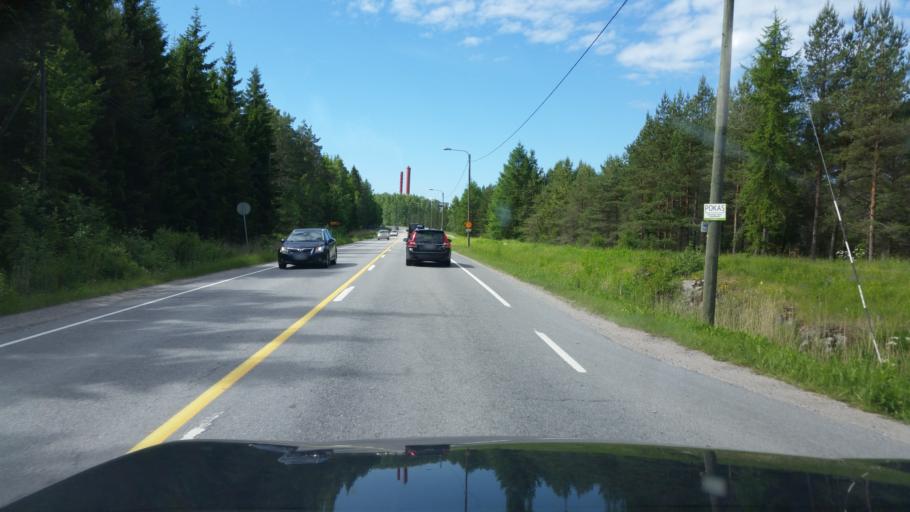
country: FI
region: Varsinais-Suomi
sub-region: Aboland-Turunmaa
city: Laensi-Turunmaa
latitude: 60.3009
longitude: 22.2771
